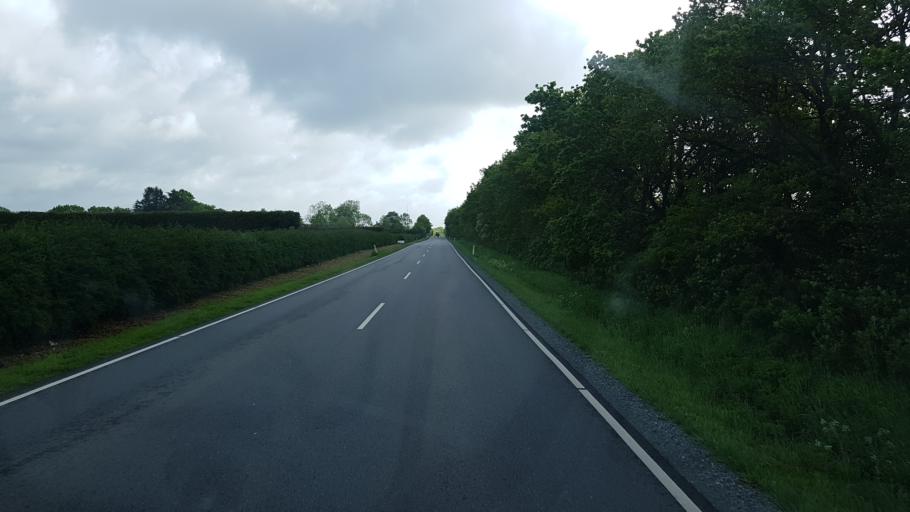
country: DK
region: South Denmark
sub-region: Vejen Kommune
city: Vejen
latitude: 55.4600
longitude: 9.1662
